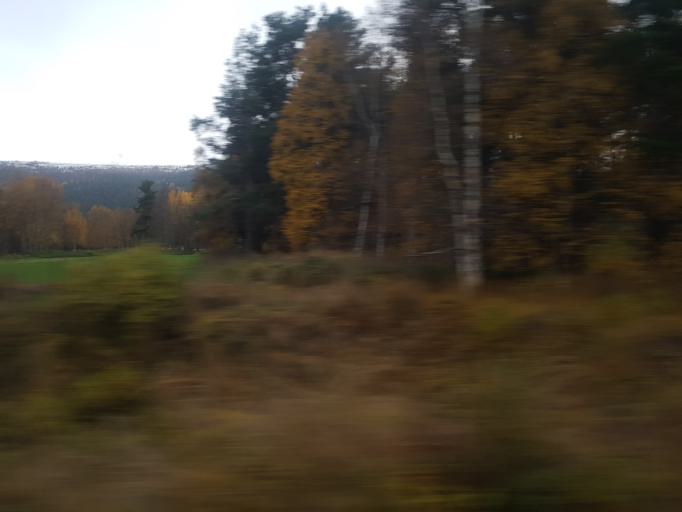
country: NO
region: Oppland
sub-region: Dovre
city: Dovre
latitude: 61.9656
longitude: 9.2638
